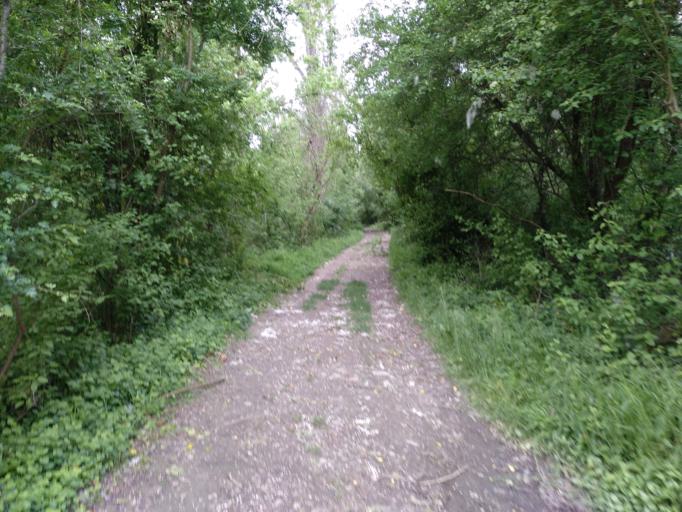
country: FR
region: Rhone-Alpes
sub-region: Departement du Rhone
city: Vernaison
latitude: 45.6374
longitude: 4.8168
